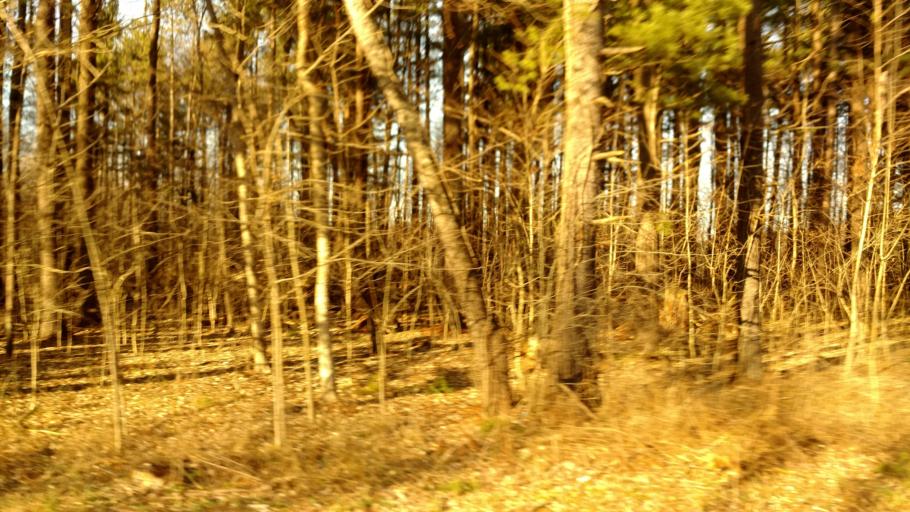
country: US
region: Ohio
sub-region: Richland County
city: Ontario
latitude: 40.7256
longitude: -82.6525
